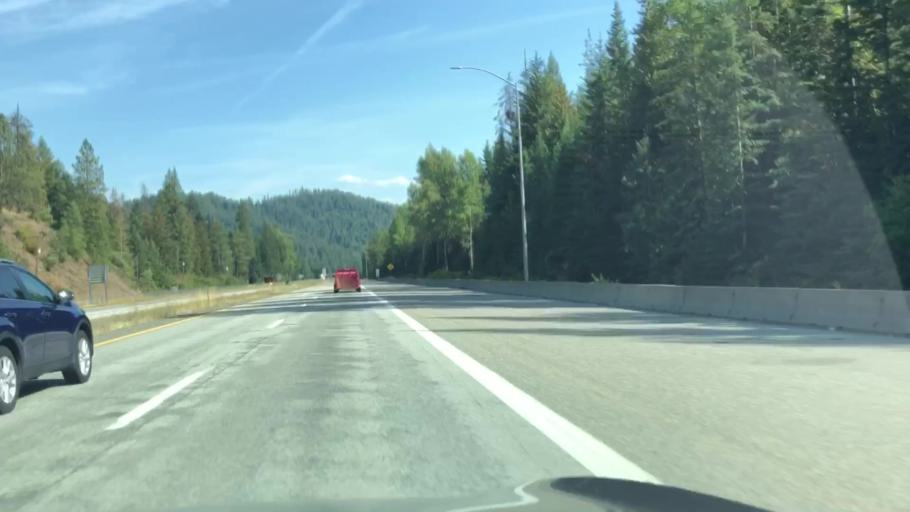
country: US
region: Idaho
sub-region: Shoshone County
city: Pinehurst
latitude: 47.5794
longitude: -116.4588
